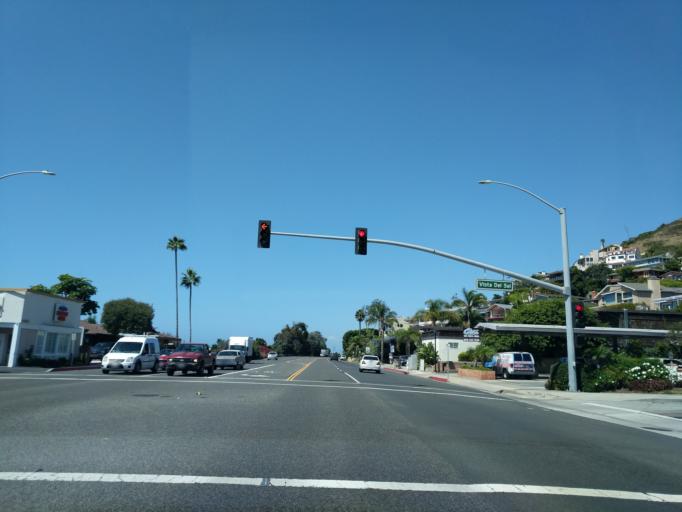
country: US
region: California
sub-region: Orange County
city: Laguna Niguel
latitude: 33.4927
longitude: -117.7348
